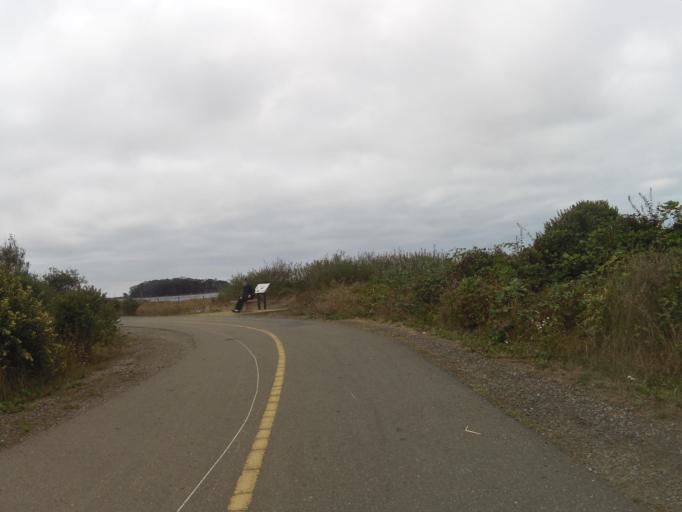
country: US
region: California
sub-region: Humboldt County
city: Bayview
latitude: 40.7806
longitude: -124.1923
